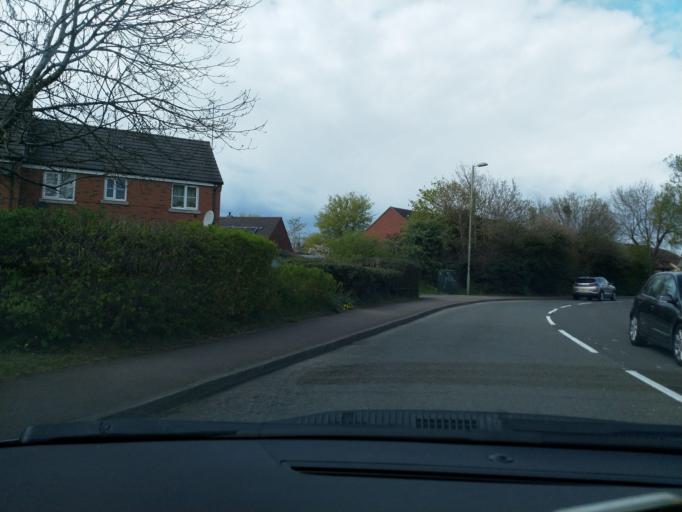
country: GB
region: England
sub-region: Suffolk
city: Woodbridge
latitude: 52.0667
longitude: 1.3209
